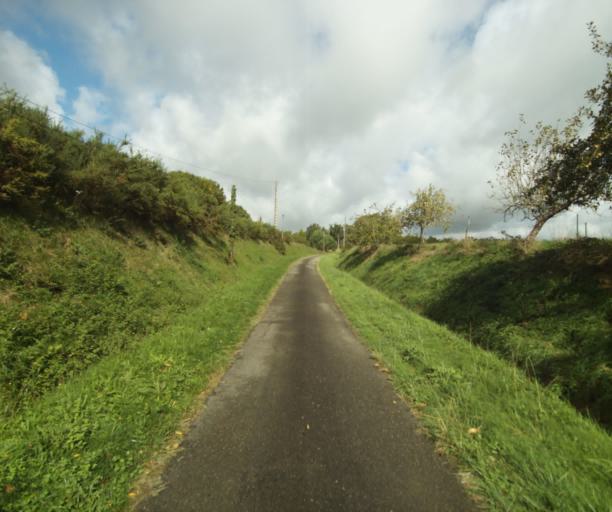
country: FR
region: Midi-Pyrenees
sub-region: Departement du Gers
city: Nogaro
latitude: 43.8345
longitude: -0.0930
